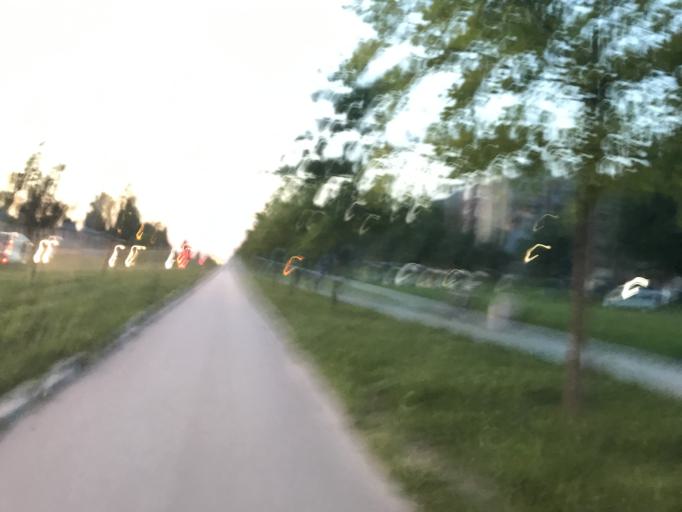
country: RS
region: Autonomna Pokrajina Vojvodina
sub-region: Juznobacki Okrug
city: Novi Sad
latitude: 45.2641
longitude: 19.8063
